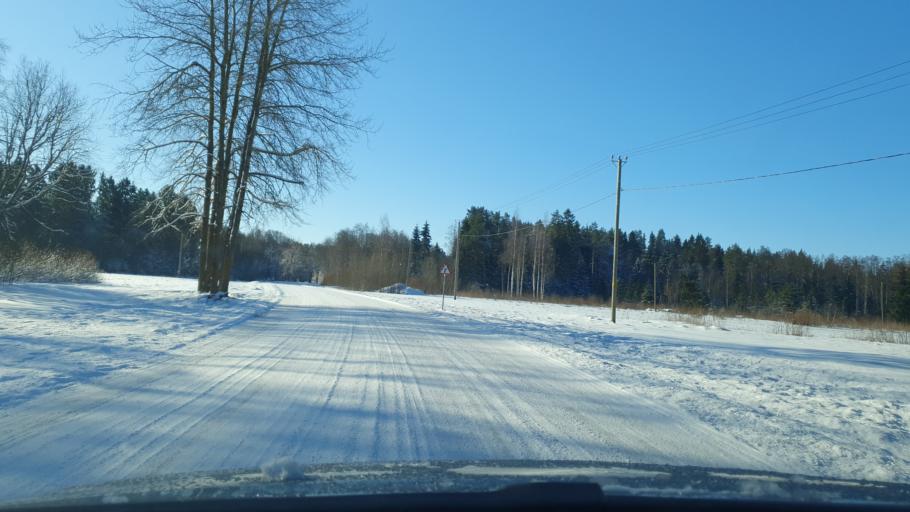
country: EE
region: Harju
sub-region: Kuusalu vald
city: Kuusalu
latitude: 59.4794
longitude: 25.4114
